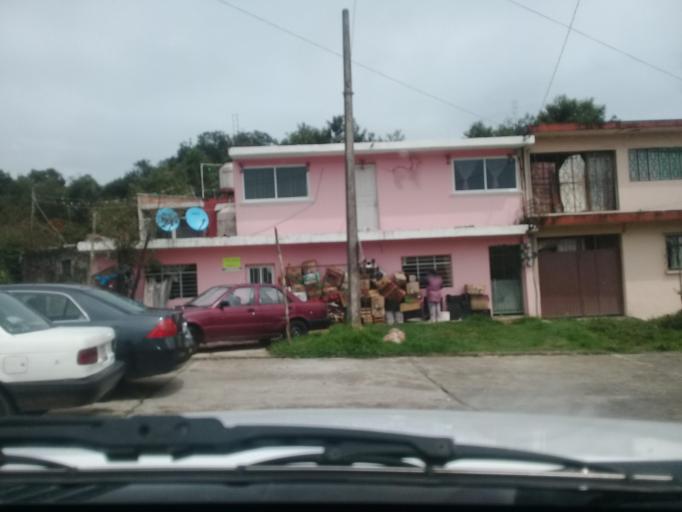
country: MX
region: Veracruz
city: Rafael Lucio
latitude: 19.5920
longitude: -96.9916
